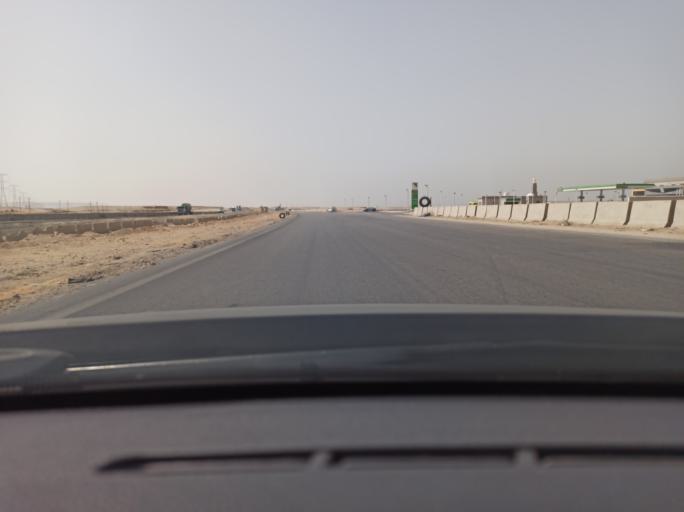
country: EG
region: Muhafazat al Fayyum
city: Al Wasitah
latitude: 29.3834
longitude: 31.3149
